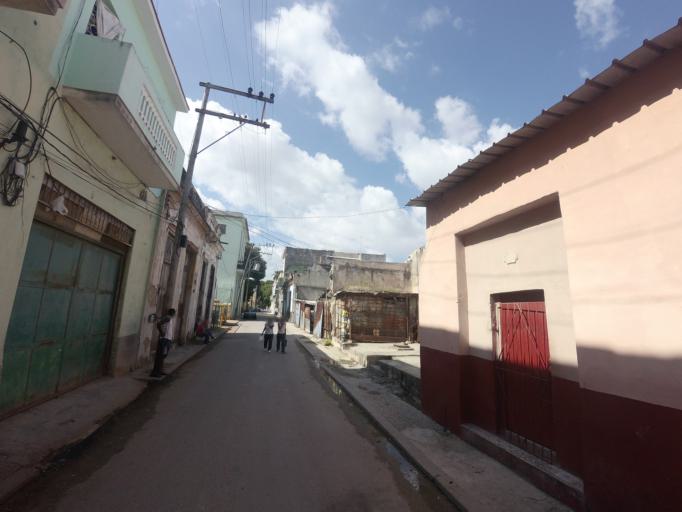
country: CU
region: La Habana
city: La Habana Vieja
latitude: 23.1300
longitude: -82.3513
